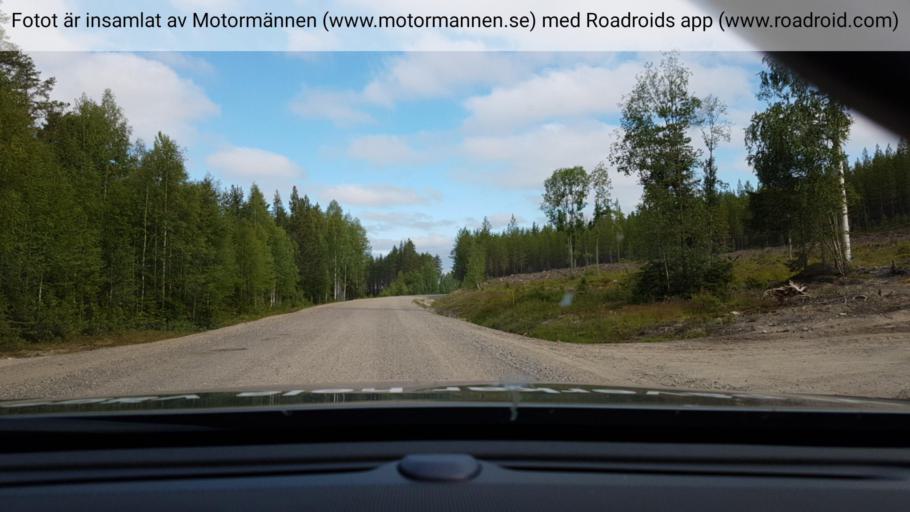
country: SE
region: Vaesterbotten
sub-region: Norsjo Kommun
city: Norsjoe
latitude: 64.6218
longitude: 19.2866
